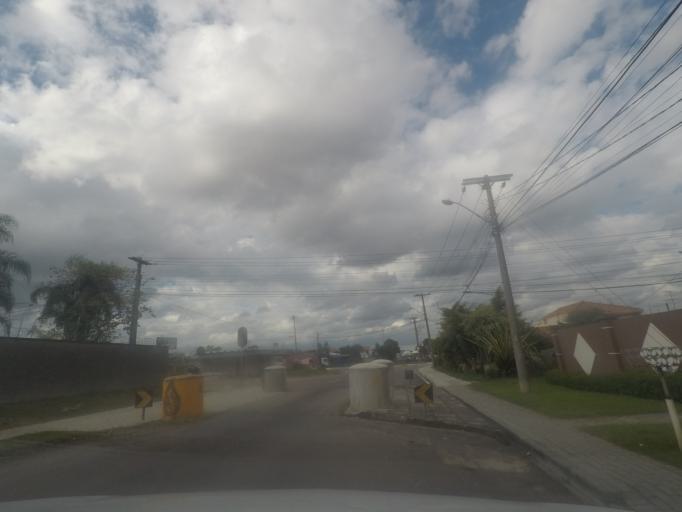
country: BR
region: Parana
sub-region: Pinhais
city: Pinhais
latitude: -25.4642
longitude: -49.2182
